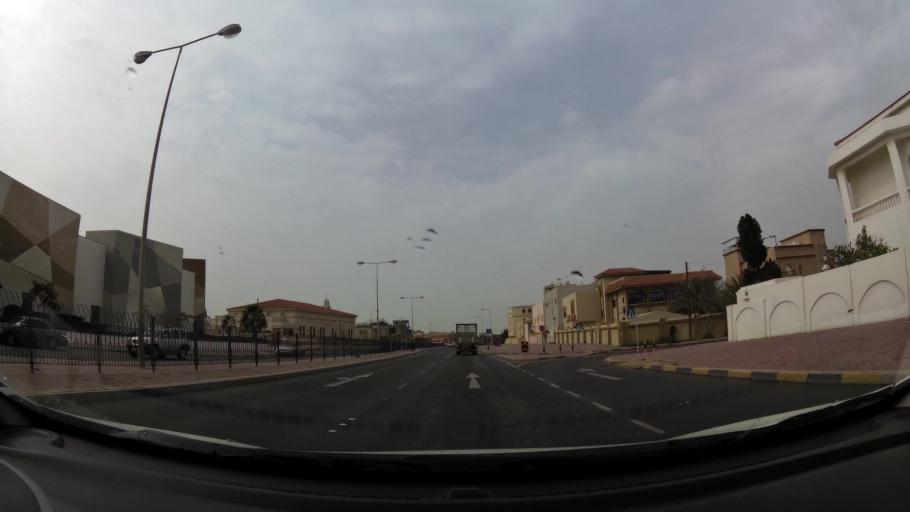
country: BH
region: Northern
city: Ar Rifa'
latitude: 26.1376
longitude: 50.5594
